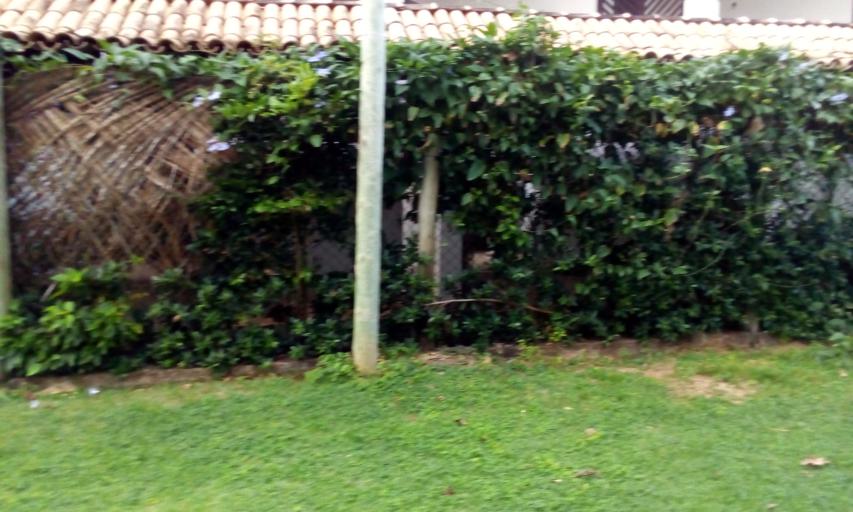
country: BR
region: Bahia
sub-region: Mata De Sao Joao
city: Mata de Sao Joao
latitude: -12.5793
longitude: -38.0057
